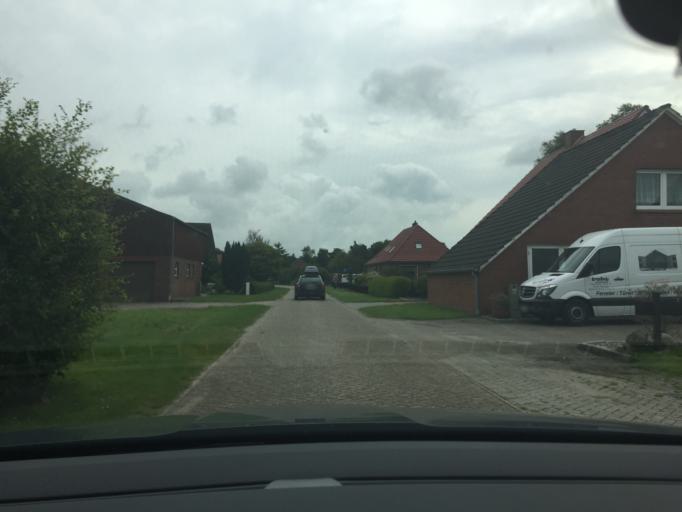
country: DE
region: Lower Saxony
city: Aurich
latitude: 53.4477
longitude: 7.5027
